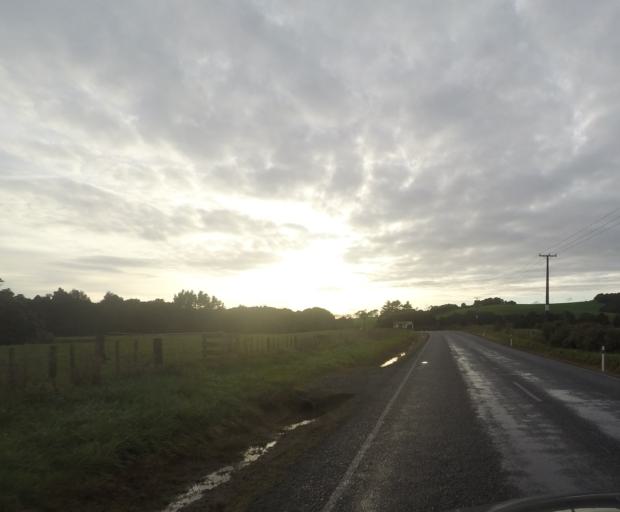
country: NZ
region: Auckland
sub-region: Auckland
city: Wellsford
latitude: -36.2190
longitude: 174.5822
